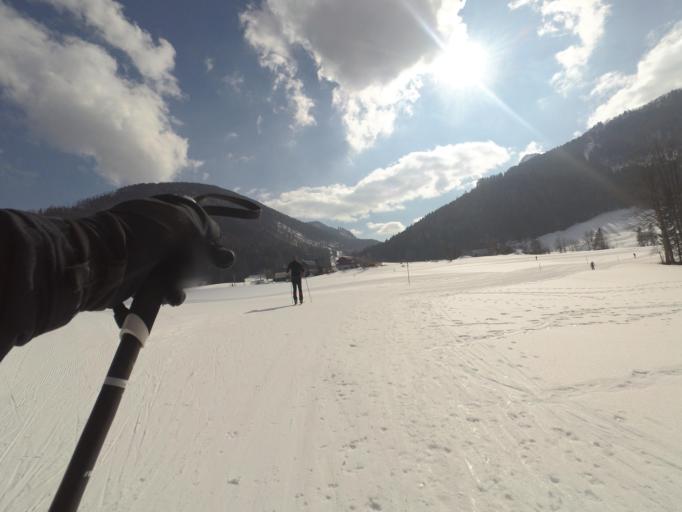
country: AT
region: Salzburg
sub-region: Politischer Bezirk Salzburg-Umgebung
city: Fuschl am See
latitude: 47.7673
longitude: 13.3199
